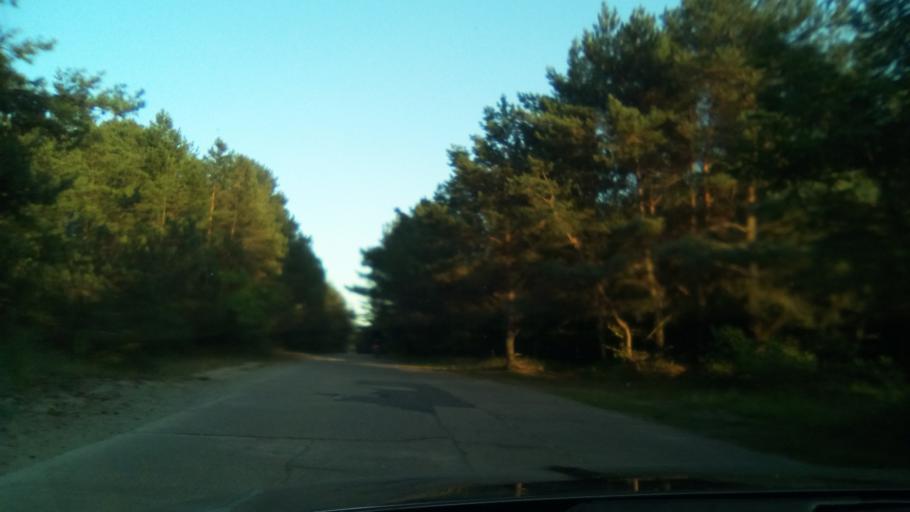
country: PL
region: West Pomeranian Voivodeship
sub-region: Swinoujscie
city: Swinoujscie
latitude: 53.9182
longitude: 14.2933
